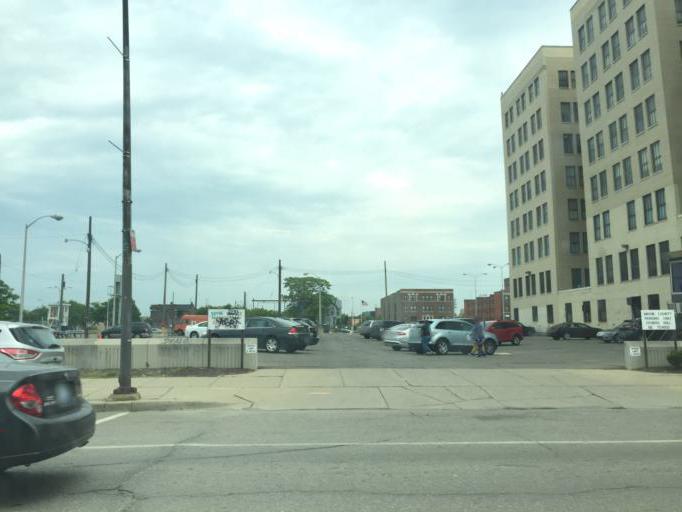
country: US
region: Michigan
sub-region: Wayne County
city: Detroit
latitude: 42.3407
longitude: -83.0621
